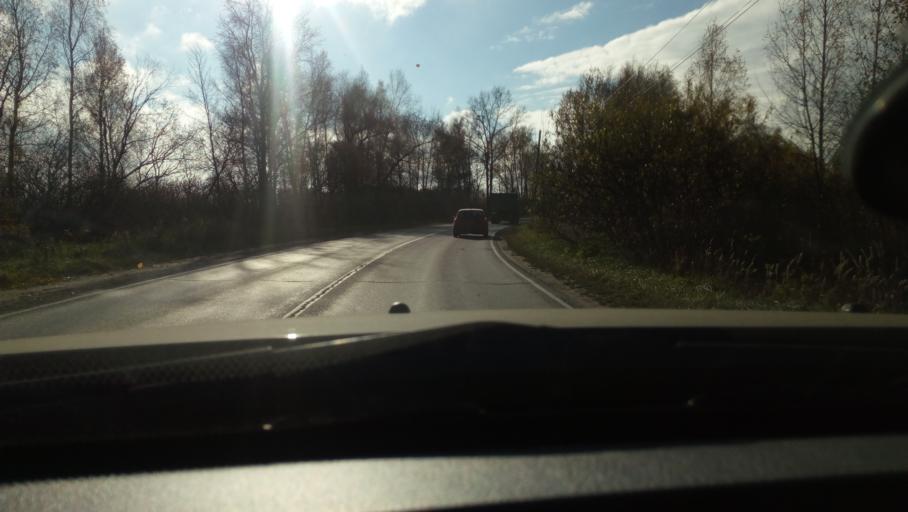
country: RU
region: Moskovskaya
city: Fryazevo
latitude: 55.7199
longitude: 38.4681
